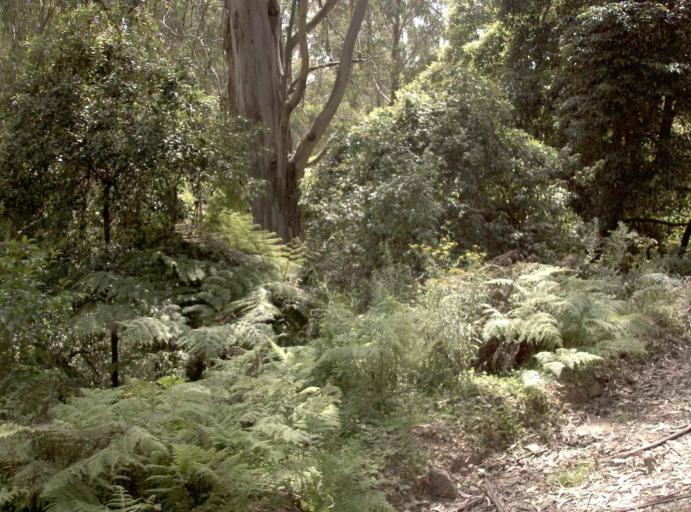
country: AU
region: Victoria
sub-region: East Gippsland
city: Lakes Entrance
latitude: -37.6204
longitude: 148.7002
